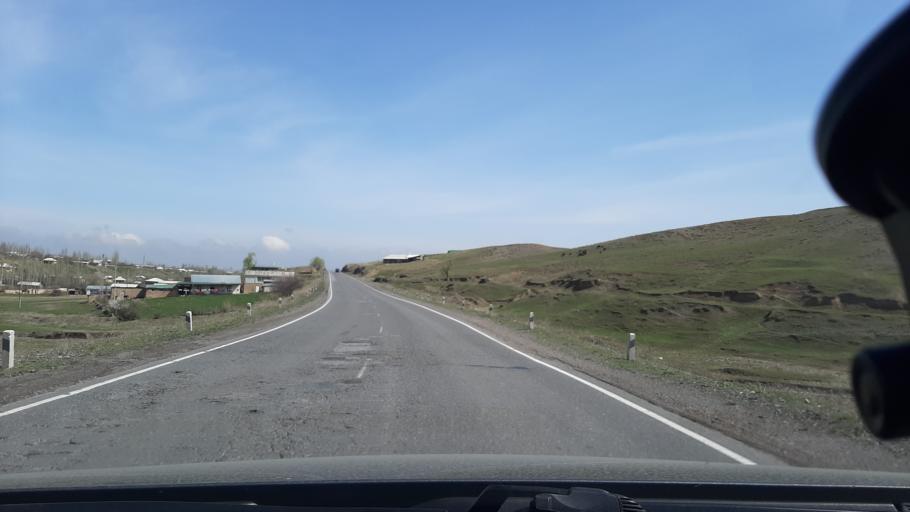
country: TJ
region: Viloyati Sughd
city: Shahriston
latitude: 39.7641
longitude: 68.8175
